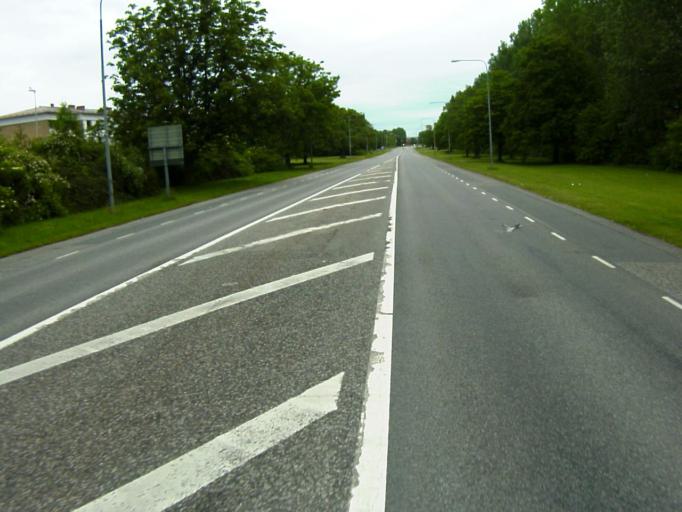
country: SE
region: Skane
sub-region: Kristianstads Kommun
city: Kristianstad
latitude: 56.0504
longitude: 14.1594
